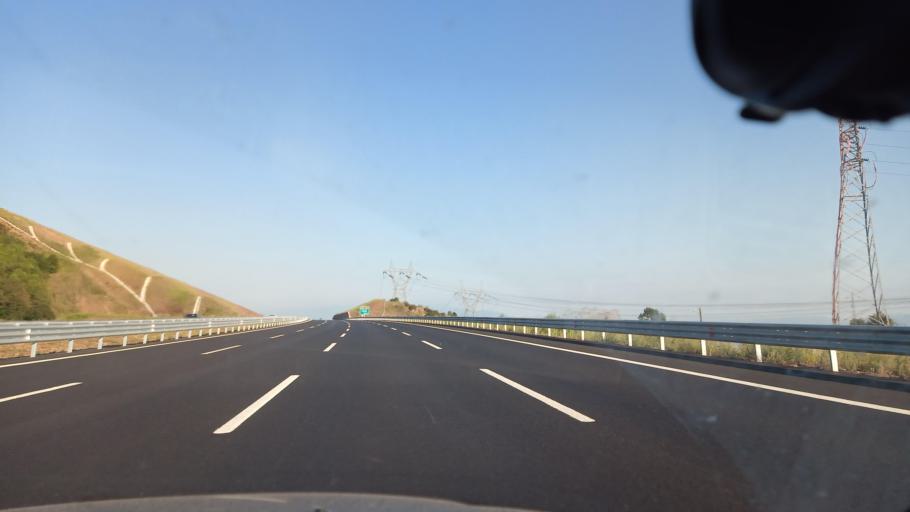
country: TR
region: Sakarya
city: Adapazari
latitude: 40.8230
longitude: 30.3998
